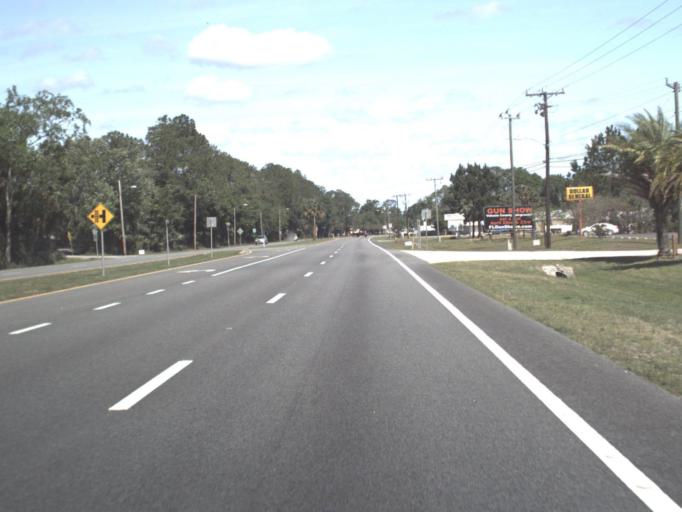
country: US
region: Florida
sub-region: Flagler County
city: Bunnell
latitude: 29.4561
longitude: -81.2491
